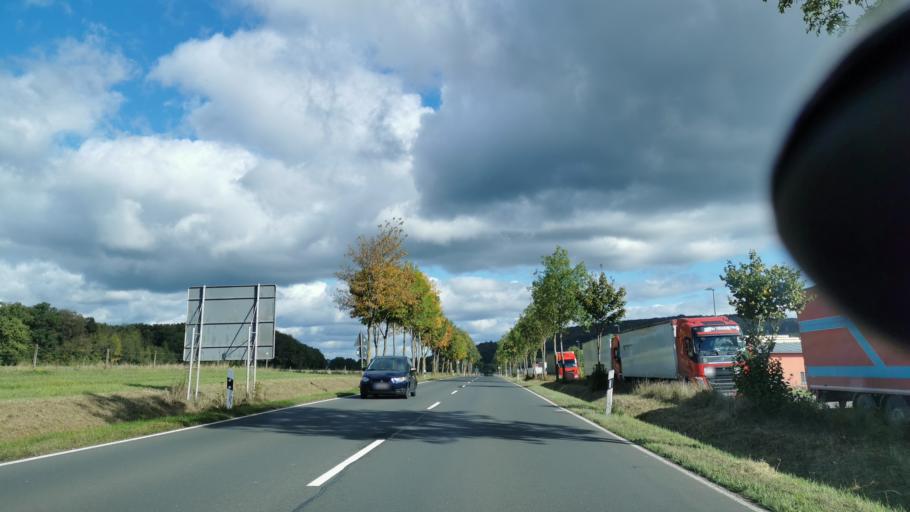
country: DE
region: Rheinland-Pfalz
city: Walsdorf
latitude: 50.2845
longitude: 6.7038
